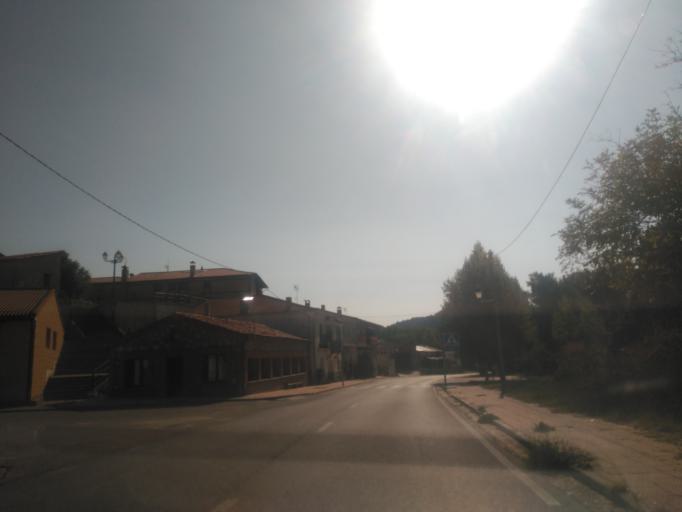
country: ES
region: Castille and Leon
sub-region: Provincia de Soria
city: Casarejos
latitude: 41.7958
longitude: -3.0323
